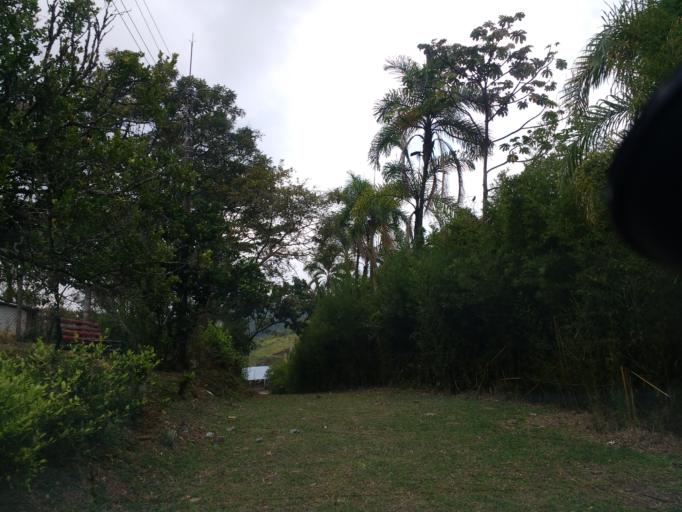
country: CO
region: Cauca
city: Santander de Quilichao
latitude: 2.9109
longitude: -76.4825
